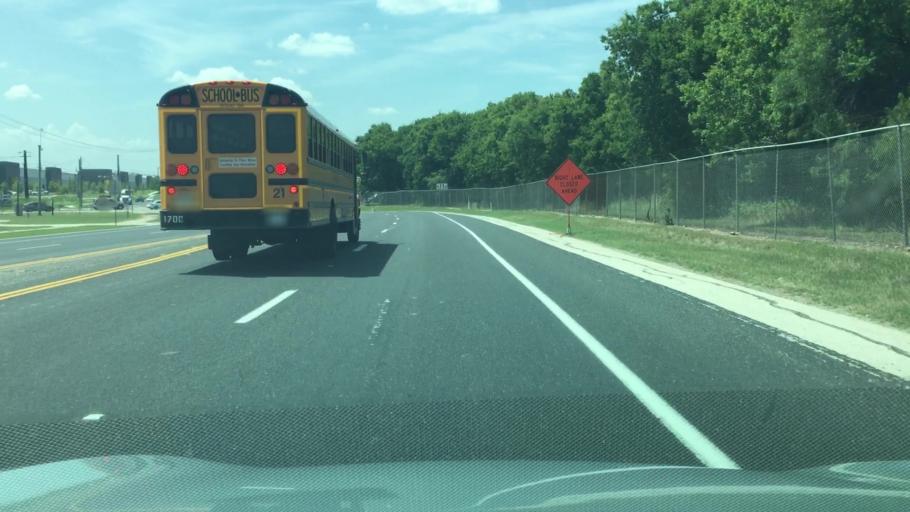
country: US
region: Texas
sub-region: Travis County
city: Austin
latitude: 30.1819
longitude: -97.6863
